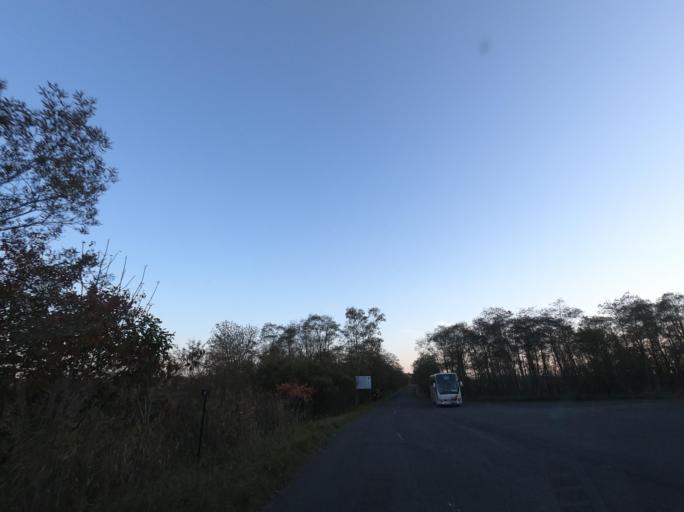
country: JP
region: Hokkaido
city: Kushiro
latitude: 43.1913
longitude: 144.4663
